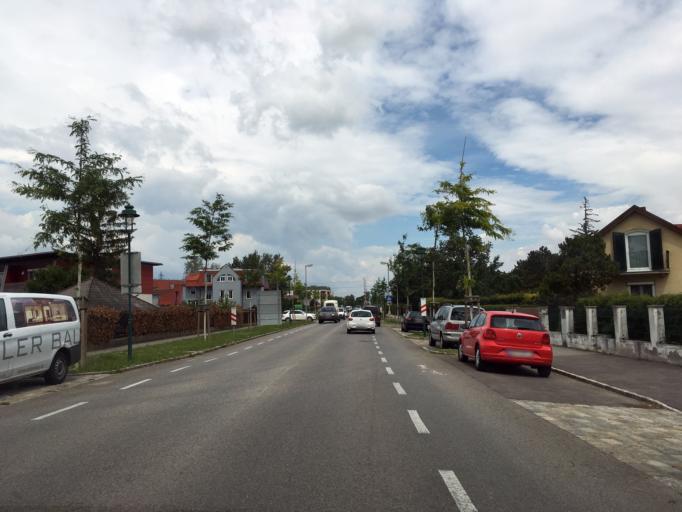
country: AT
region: Lower Austria
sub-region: Politischer Bezirk Modling
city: Laxenburg
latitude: 48.0753
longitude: 16.3529
